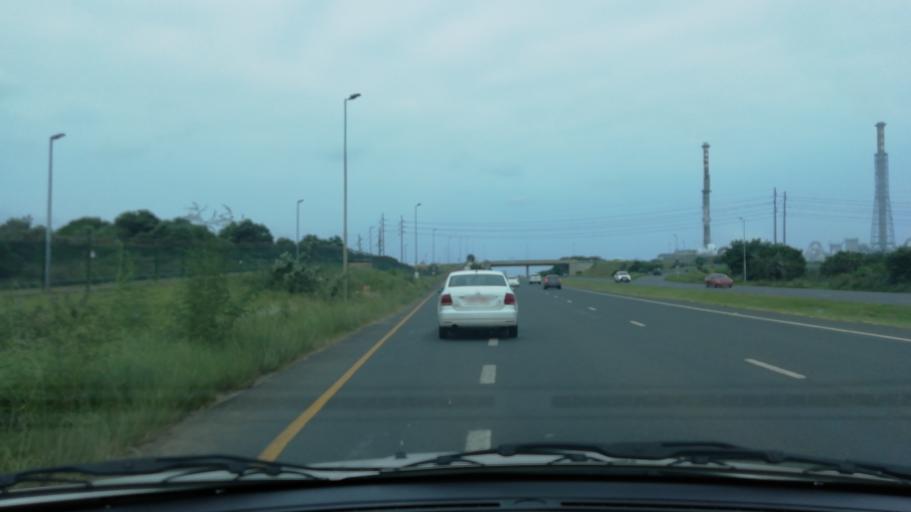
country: ZA
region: KwaZulu-Natal
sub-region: uThungulu District Municipality
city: Richards Bay
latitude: -28.7710
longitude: 32.0305
